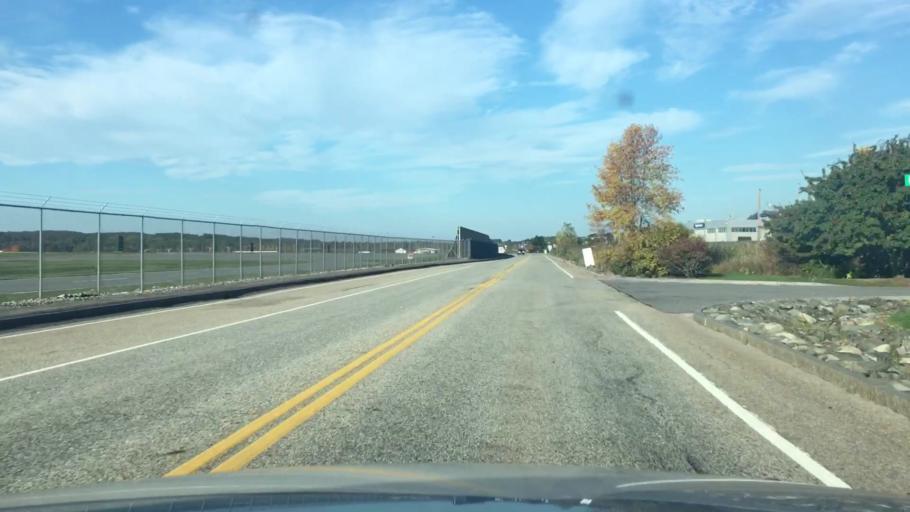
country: US
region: Maine
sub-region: Cumberland County
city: South Portland Gardens
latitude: 43.6474
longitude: -70.3218
